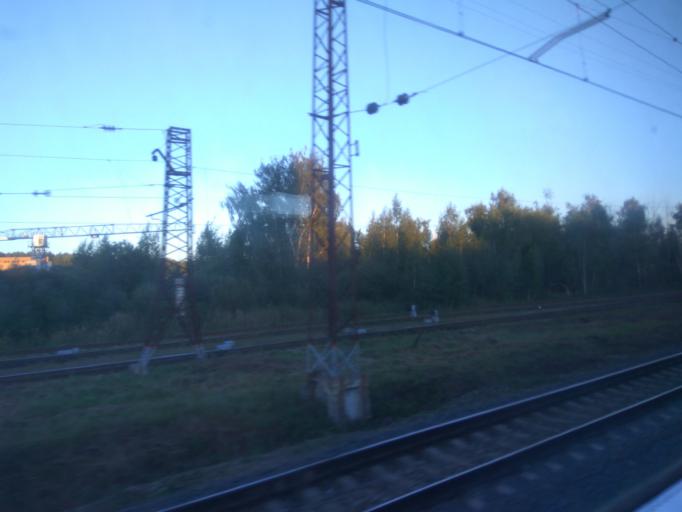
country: RU
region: Moskovskaya
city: Elektrostal'
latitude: 55.7663
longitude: 38.4696
